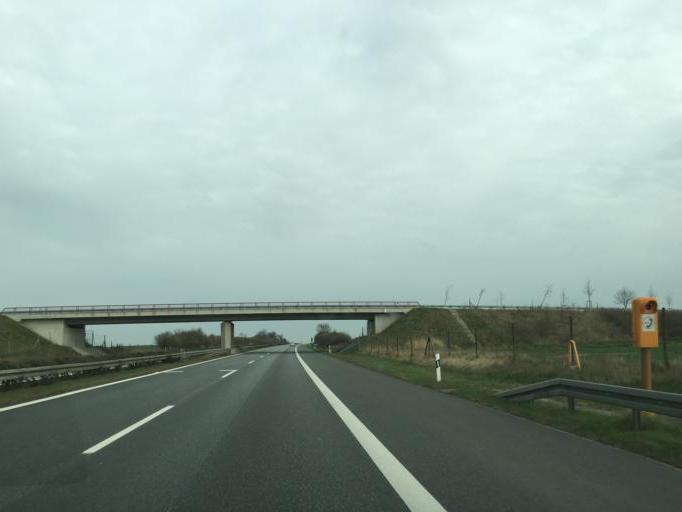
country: DE
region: Mecklenburg-Vorpommern
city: Laage
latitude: 53.8677
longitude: 12.2594
